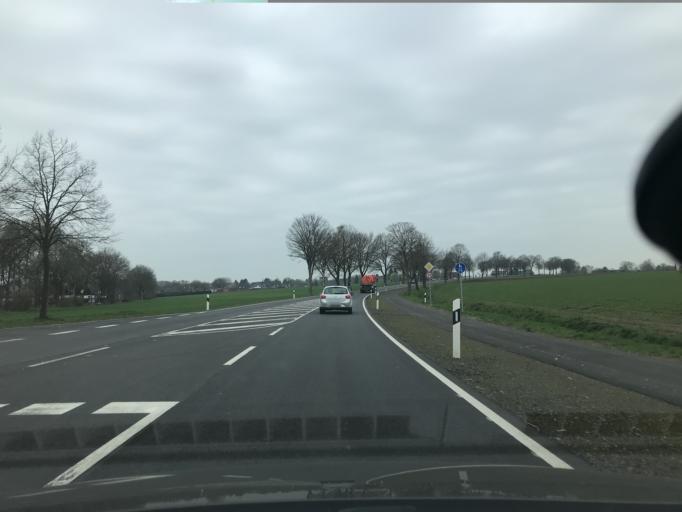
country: DE
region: North Rhine-Westphalia
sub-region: Regierungsbezirk Dusseldorf
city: Schwalmtal
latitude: 51.2350
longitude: 6.2590
